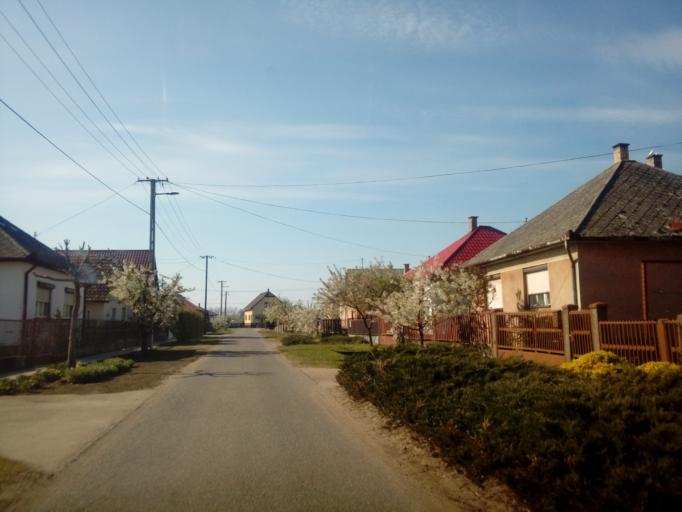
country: HU
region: Szabolcs-Szatmar-Bereg
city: Balkany
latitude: 47.7716
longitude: 21.8470
